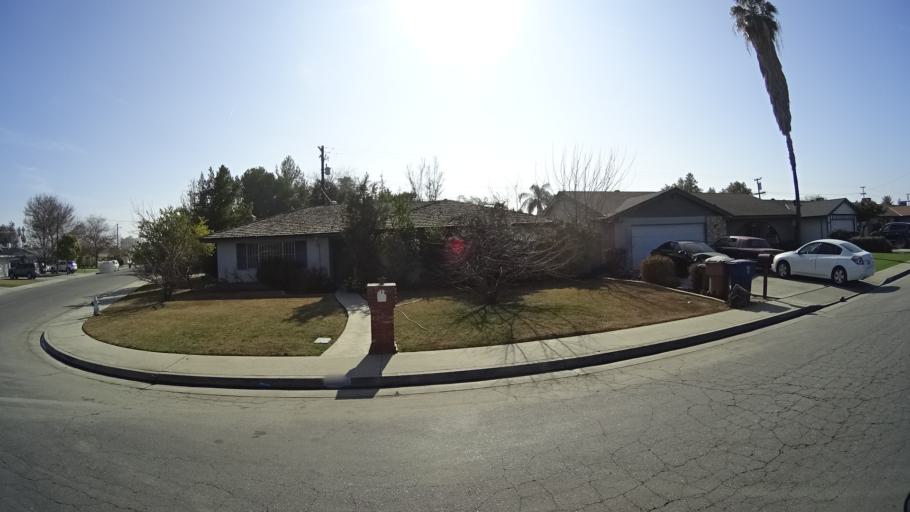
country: US
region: California
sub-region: Kern County
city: Bakersfield
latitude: 35.3377
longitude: -119.0412
